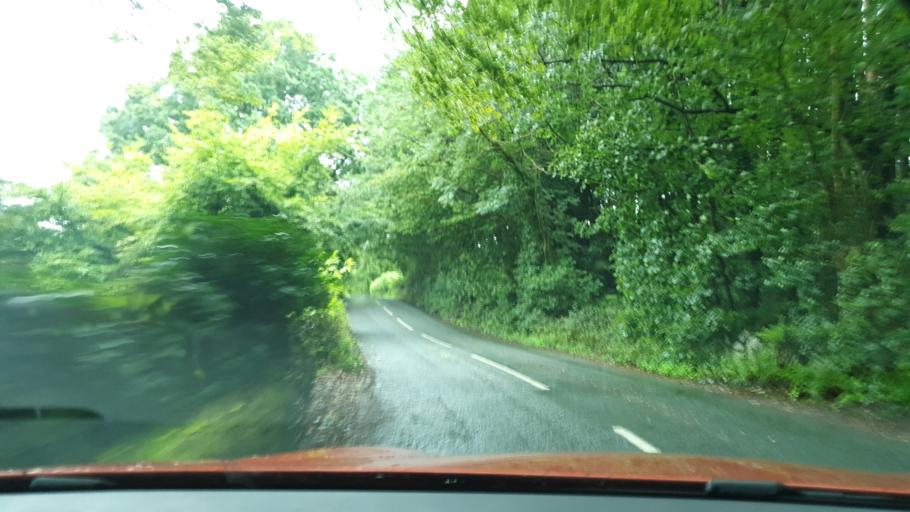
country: GB
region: England
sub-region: Cumbria
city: Ulverston
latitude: 54.2494
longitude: -3.0481
